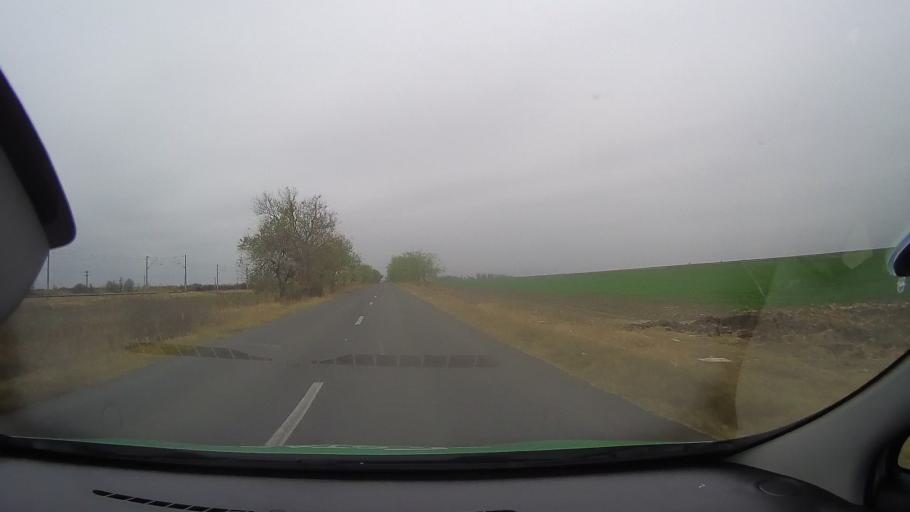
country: RO
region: Ialomita
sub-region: Comuna Valea Ciorii
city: Valea Ciorii
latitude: 44.6943
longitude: 27.6034
